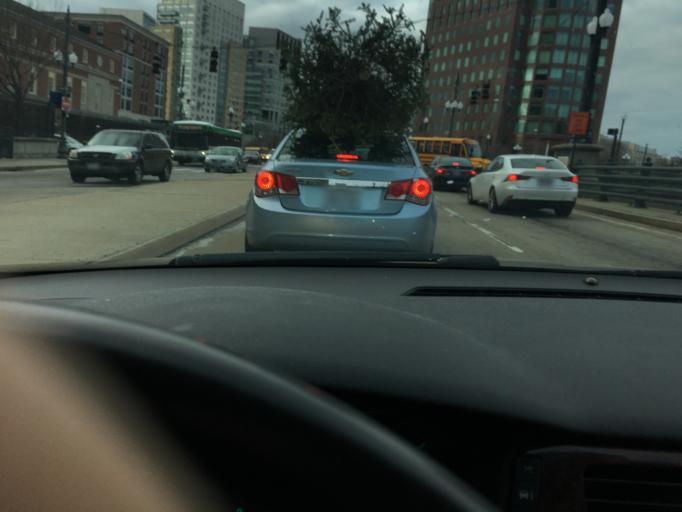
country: US
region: Rhode Island
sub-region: Providence County
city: Providence
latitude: 41.8261
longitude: -71.4098
